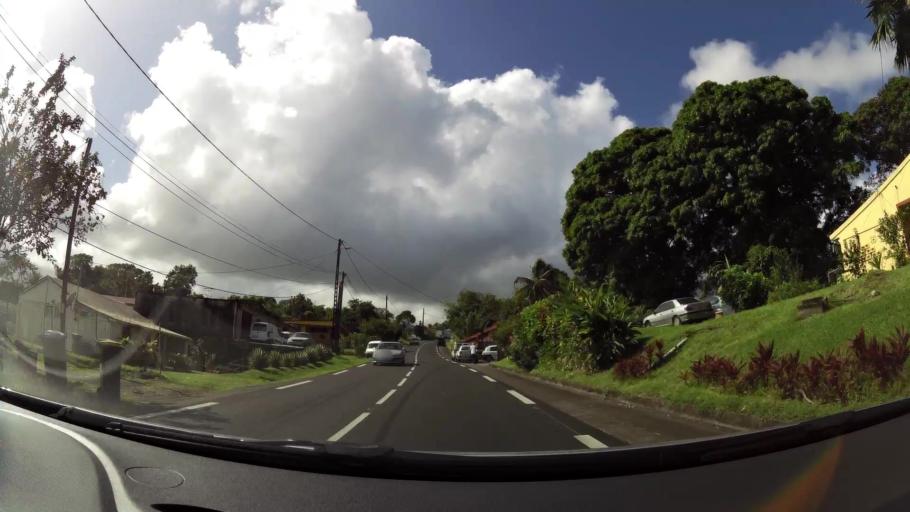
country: MQ
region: Martinique
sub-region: Martinique
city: Basse-Pointe
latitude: 14.8315
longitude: -61.1053
